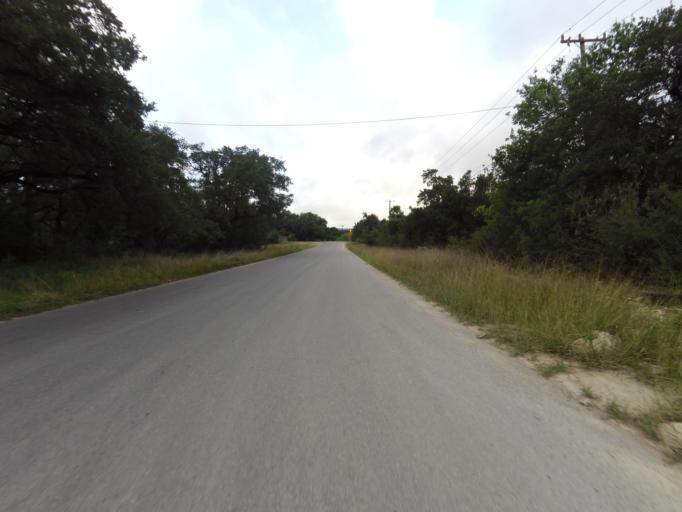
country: US
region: Texas
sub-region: Bexar County
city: Shavano Park
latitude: 29.5949
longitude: -98.6018
